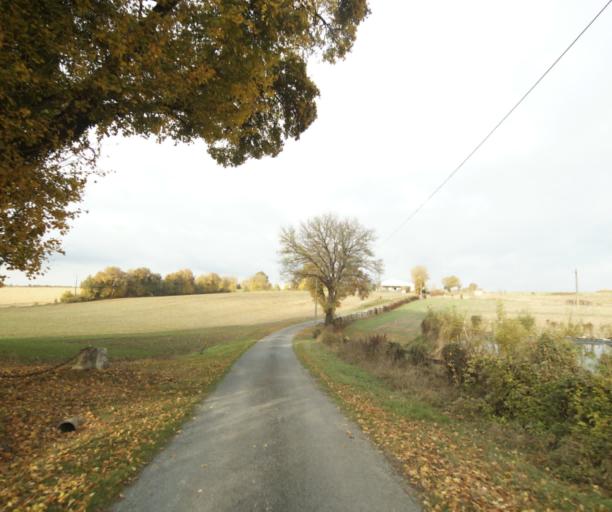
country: FR
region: Poitou-Charentes
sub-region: Departement de la Charente-Maritime
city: Nieul-les-Saintes
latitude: 45.7829
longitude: -0.7415
